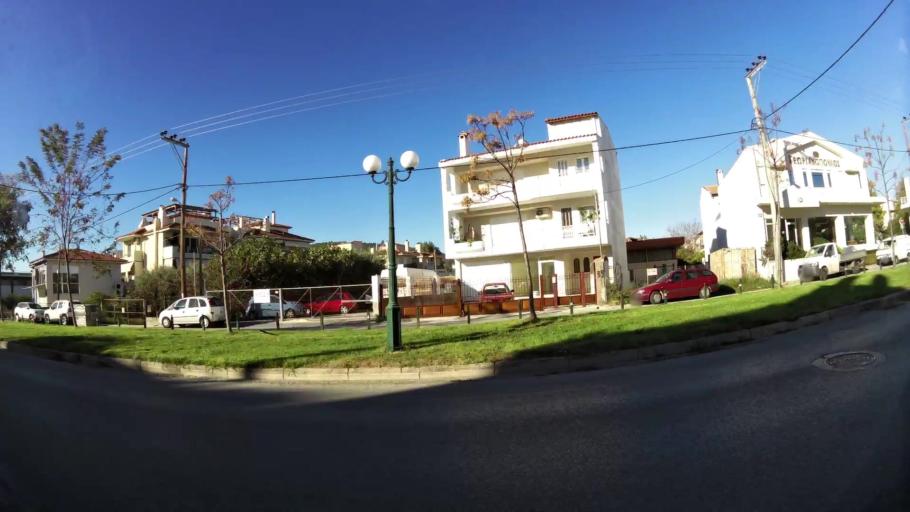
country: GR
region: Attica
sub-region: Nomarchia Anatolikis Attikis
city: Gerakas
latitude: 38.0133
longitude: 23.8539
